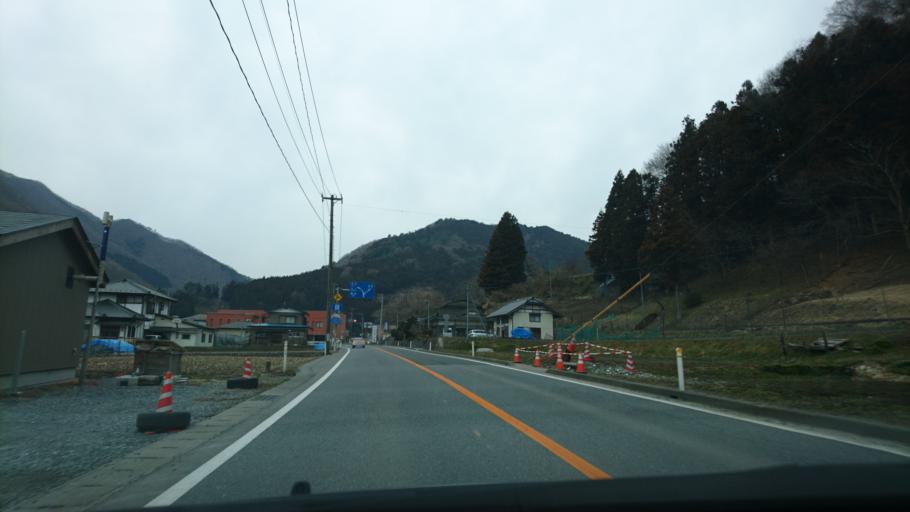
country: JP
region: Iwate
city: Tono
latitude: 39.1503
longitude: 141.5432
